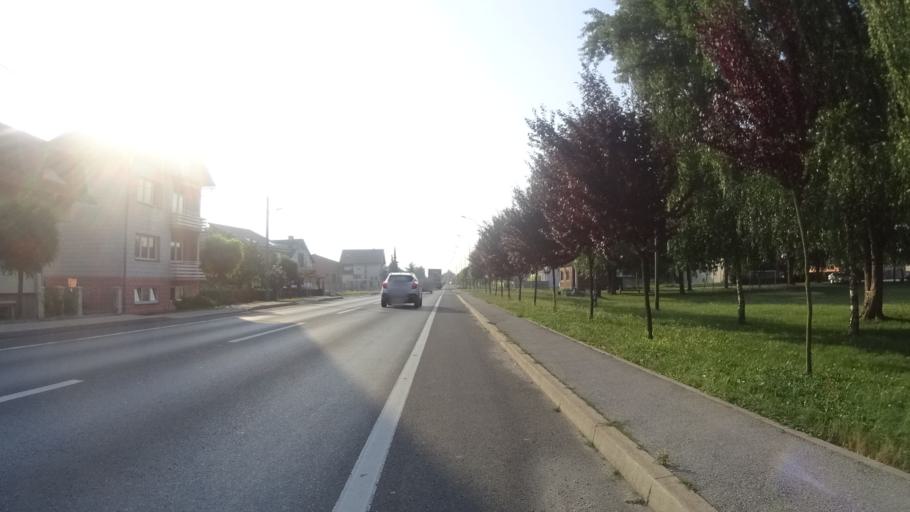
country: HR
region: Varazdinska
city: Sracinec
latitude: 46.3262
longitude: 16.2890
